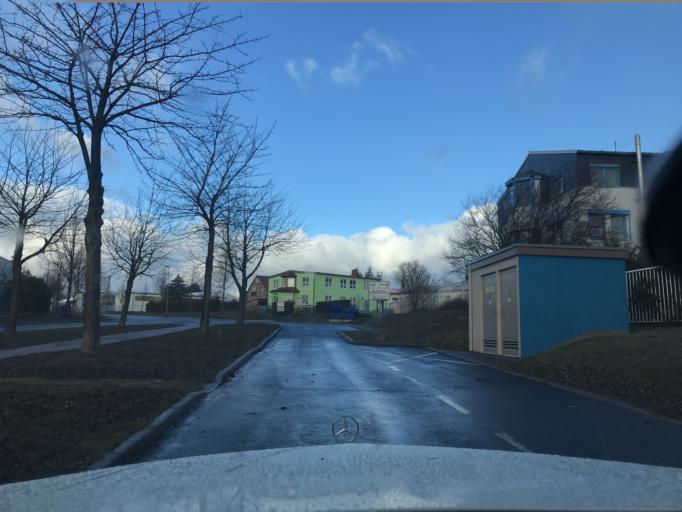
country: DE
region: Thuringia
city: Muehlhausen
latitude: 51.1983
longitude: 10.4718
